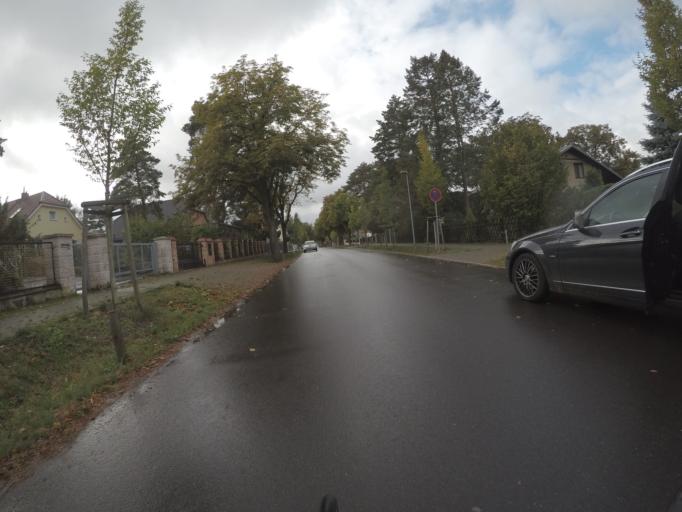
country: DE
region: Berlin
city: Blankenfelde
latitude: 52.6479
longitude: 13.3880
